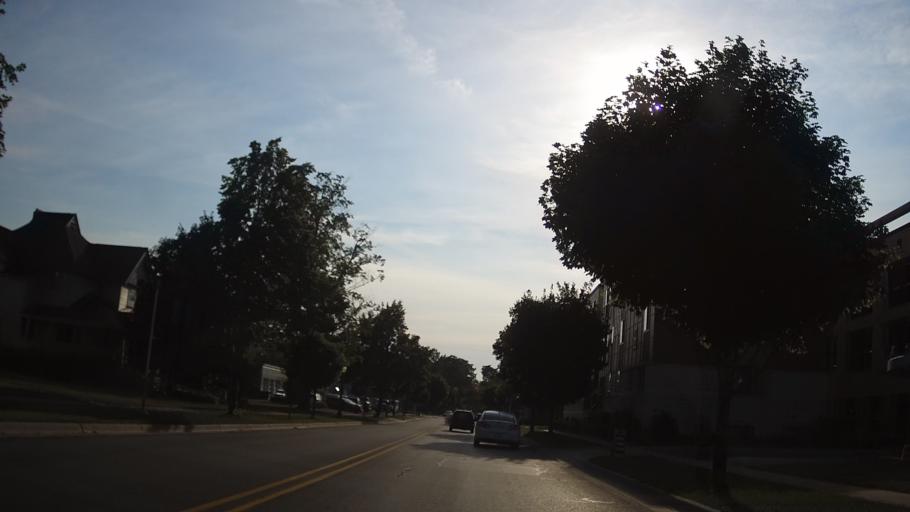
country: US
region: Michigan
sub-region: Grand Traverse County
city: Traverse City
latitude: 44.7594
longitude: -85.6219
